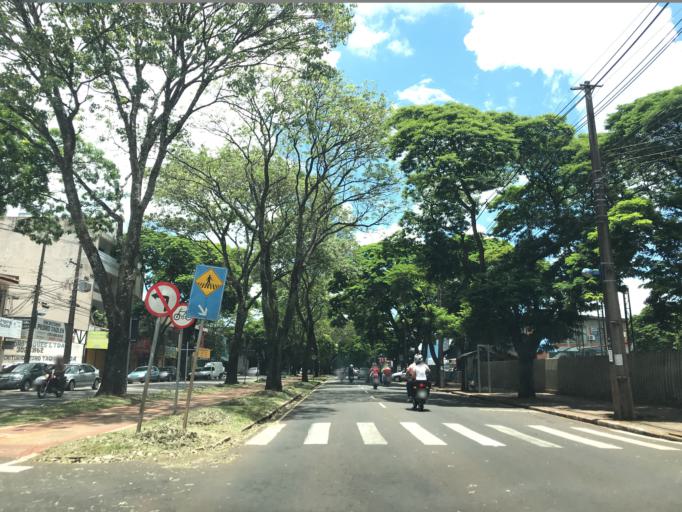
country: BR
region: Parana
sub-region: Maringa
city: Maringa
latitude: -23.4089
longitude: -51.9236
